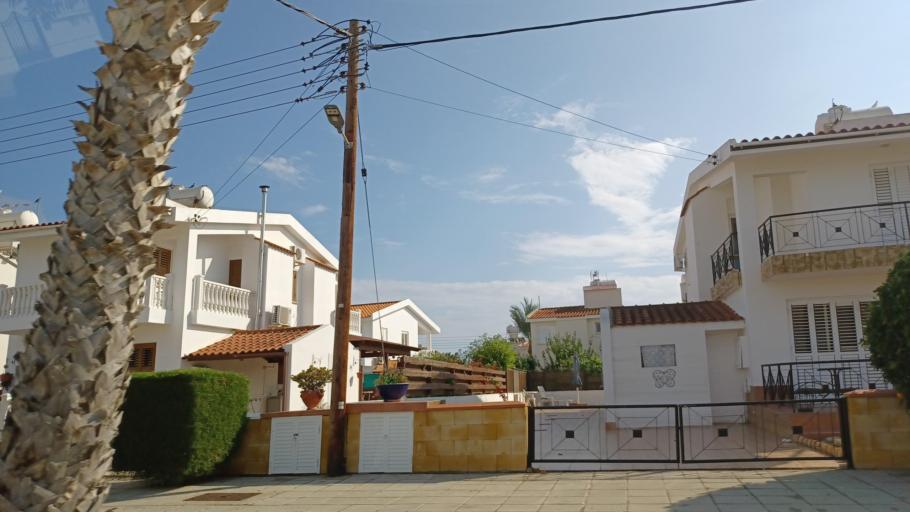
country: CY
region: Larnaka
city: Tersefanou
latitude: 34.7902
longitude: 33.4998
